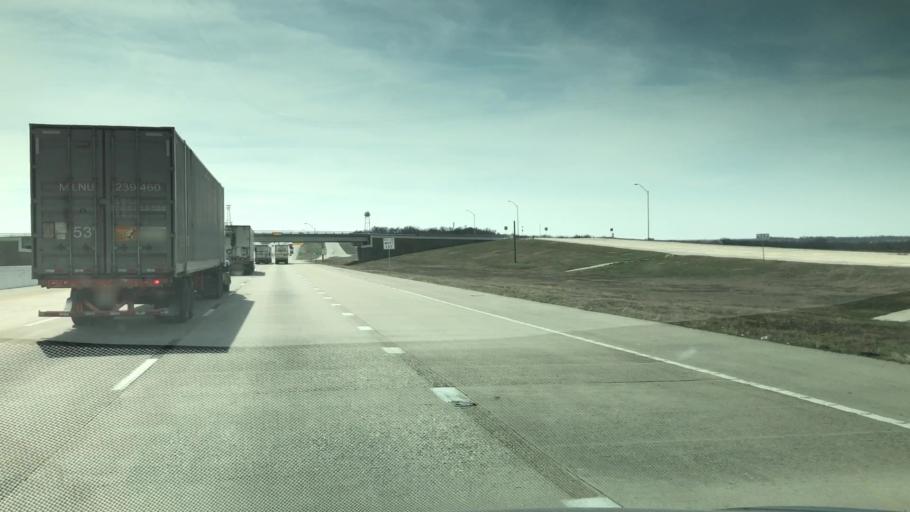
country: US
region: Texas
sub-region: McLennan County
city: West
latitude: 31.8399
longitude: -97.0893
